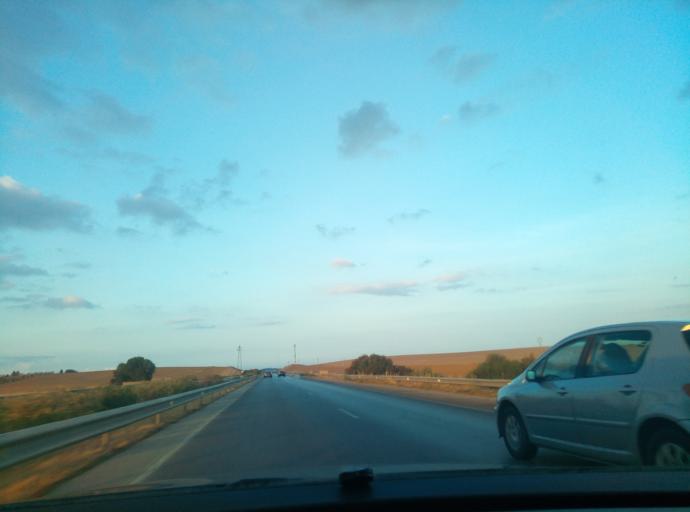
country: TN
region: Tunis
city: Oued Lill
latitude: 36.7261
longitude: 9.9971
